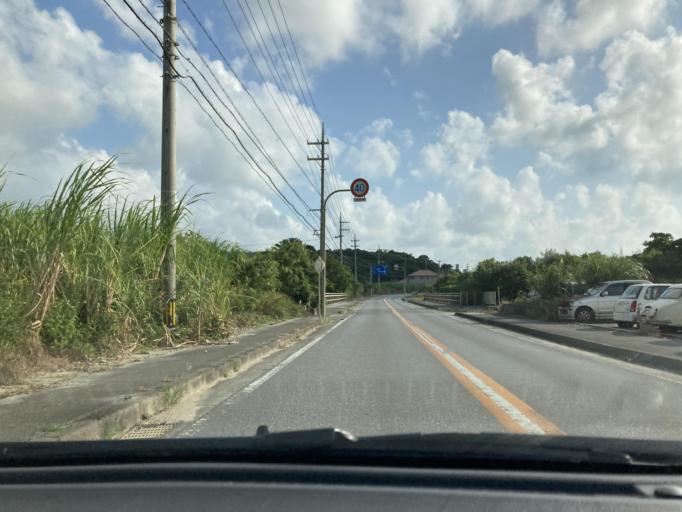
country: JP
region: Okinawa
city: Itoman
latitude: 26.1402
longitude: 127.7007
